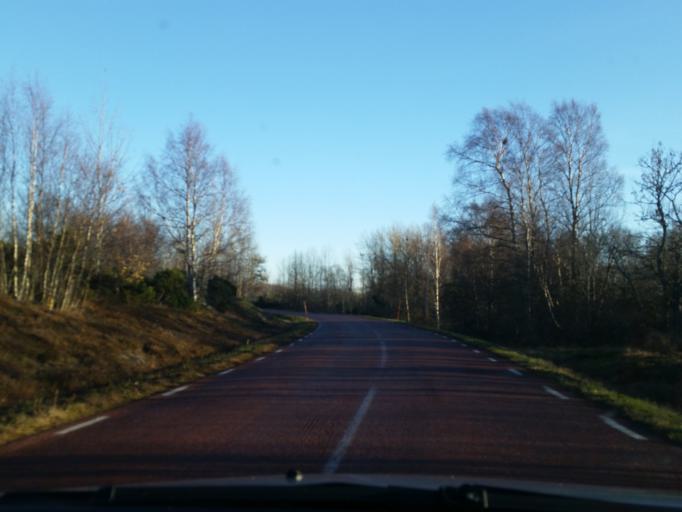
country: AX
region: Alands skaergard
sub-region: Braendoe
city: Braendoe
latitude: 60.3752
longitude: 21.0388
